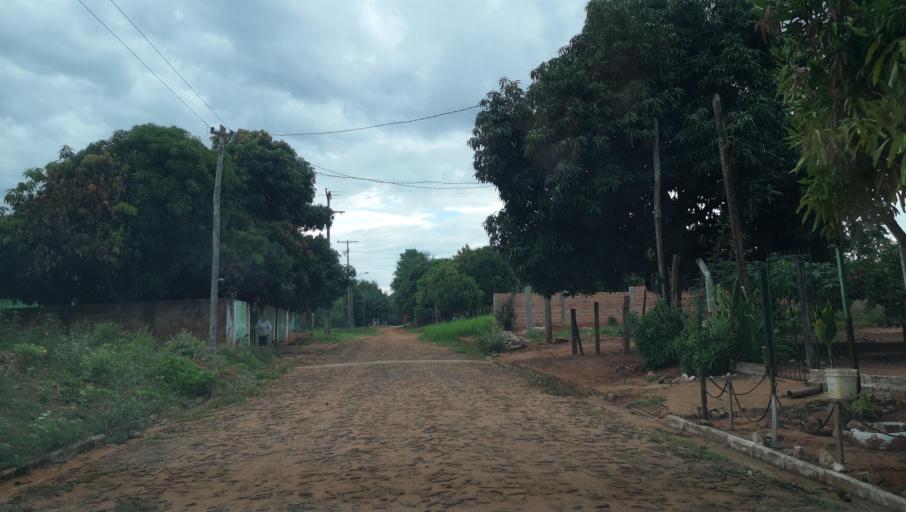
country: PY
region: San Pedro
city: Capiibary
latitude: -24.7228
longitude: -56.0178
